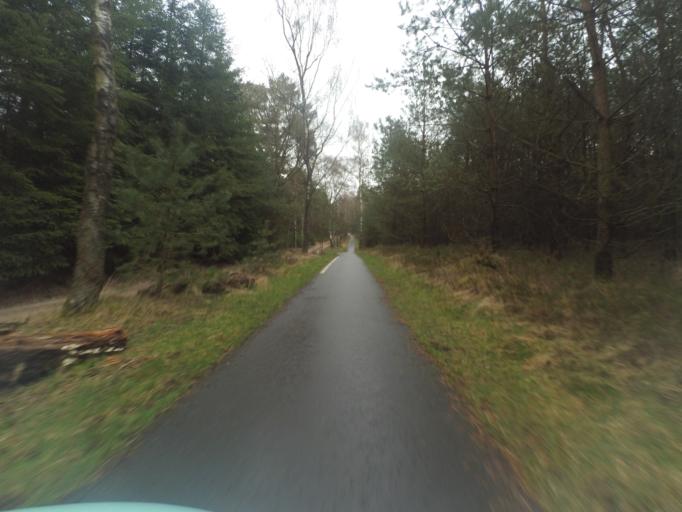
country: NL
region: Gelderland
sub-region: Gemeente Apeldoorn
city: Loenen
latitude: 52.0722
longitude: 6.0107
